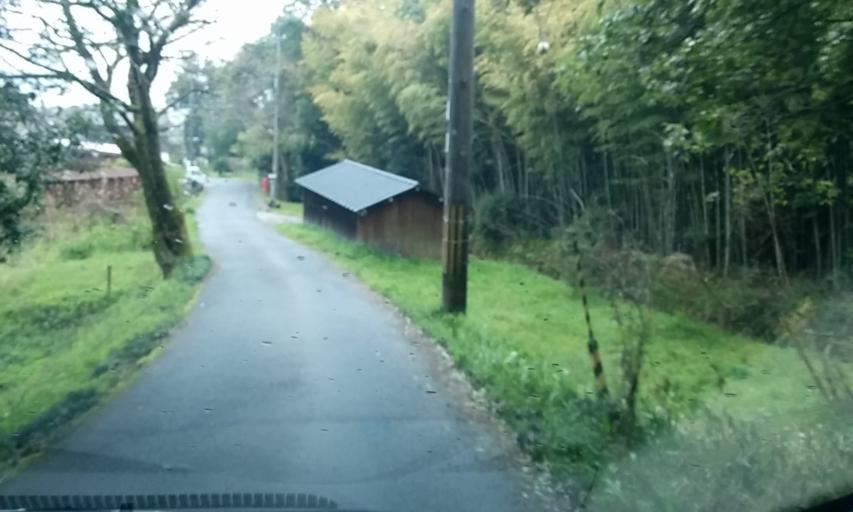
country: JP
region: Kyoto
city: Miyazu
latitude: 35.5852
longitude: 135.1985
